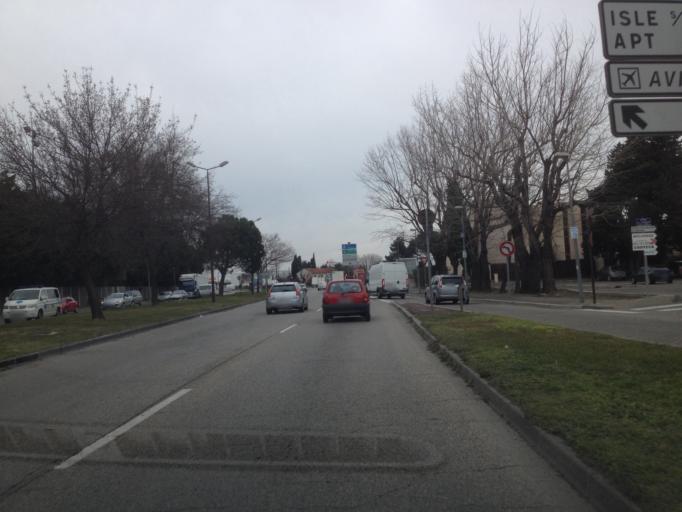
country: FR
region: Provence-Alpes-Cote d'Azur
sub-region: Departement du Vaucluse
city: Avignon
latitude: 43.9326
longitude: 4.8301
